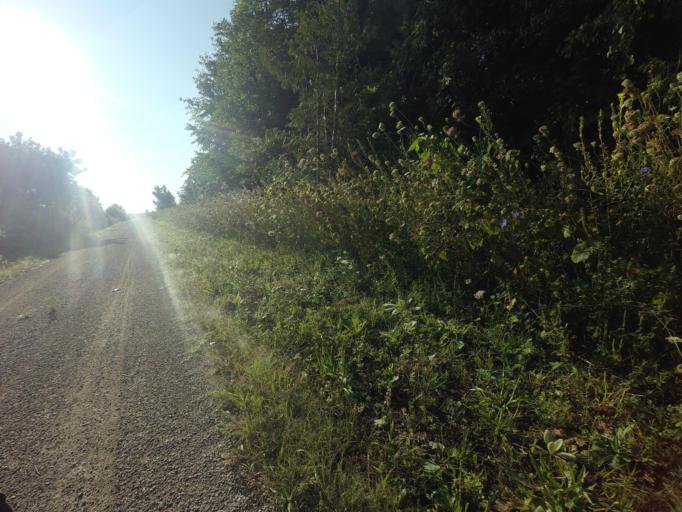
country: CA
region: Ontario
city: Goderich
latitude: 43.7638
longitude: -81.5292
